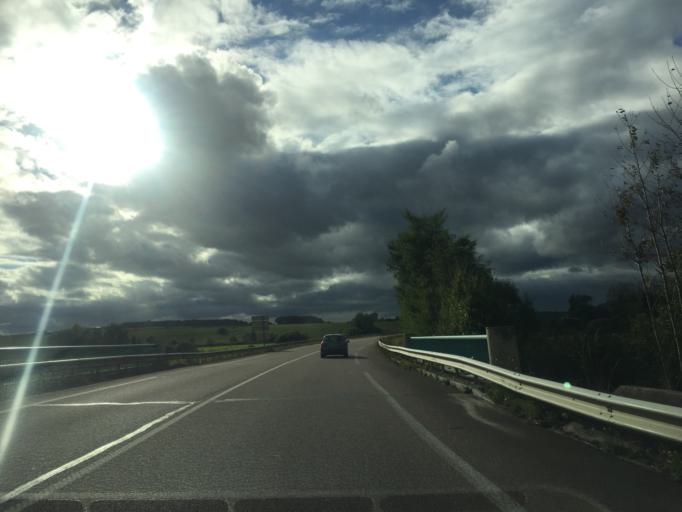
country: FR
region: Lorraine
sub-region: Departement des Vosges
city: Chatenois
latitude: 48.2922
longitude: 5.8987
